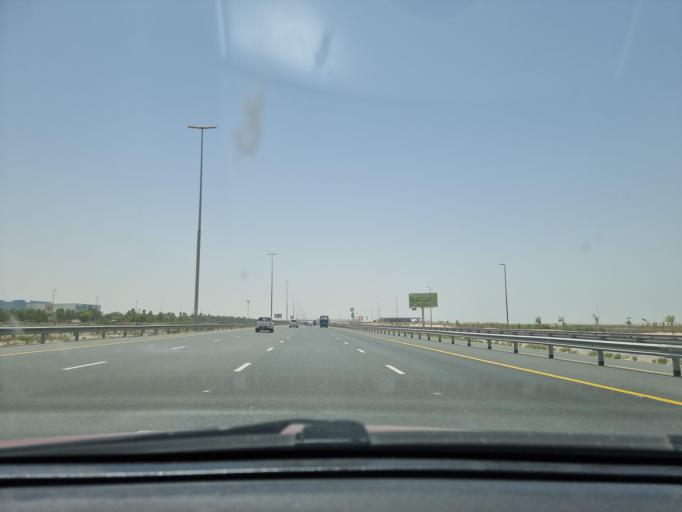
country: AE
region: Dubai
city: Dubai
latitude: 24.9285
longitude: 55.0060
